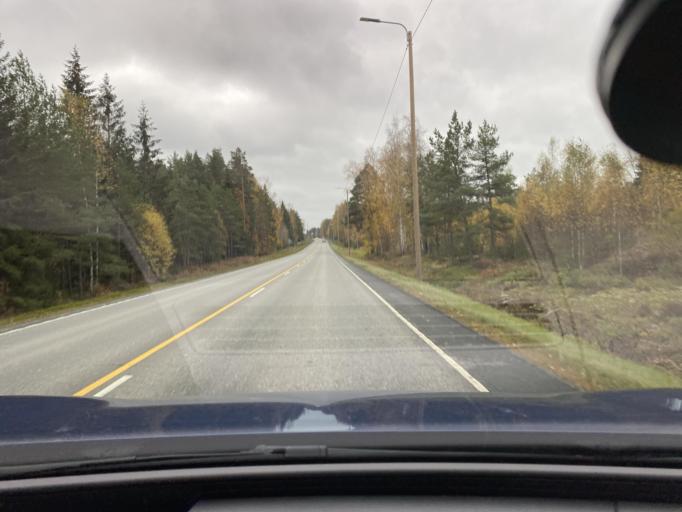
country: FI
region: Varsinais-Suomi
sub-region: Vakka-Suomi
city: Laitila
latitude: 60.9652
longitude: 21.5943
